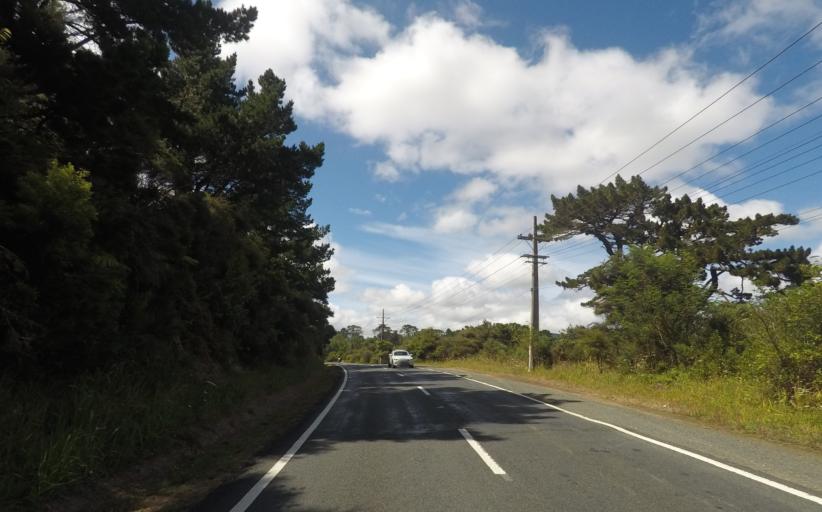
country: NZ
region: Auckland
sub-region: Auckland
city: Muriwai Beach
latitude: -36.8536
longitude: 174.5441
